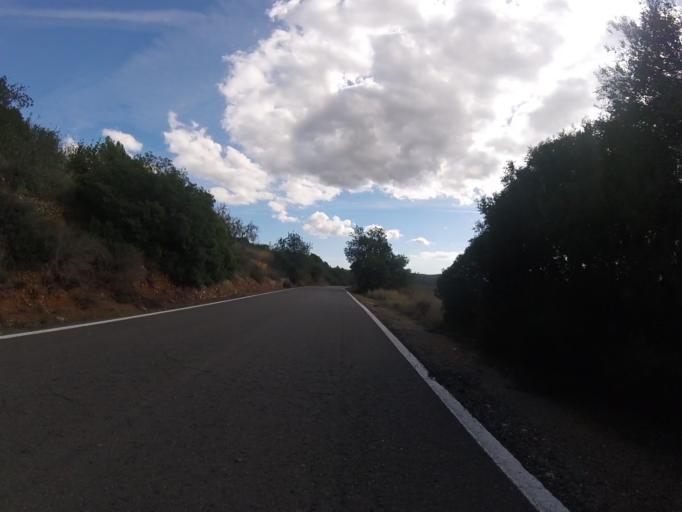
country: ES
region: Valencia
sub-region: Provincia de Castello
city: Cuevas de Vinroma
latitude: 40.3640
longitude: 0.1221
